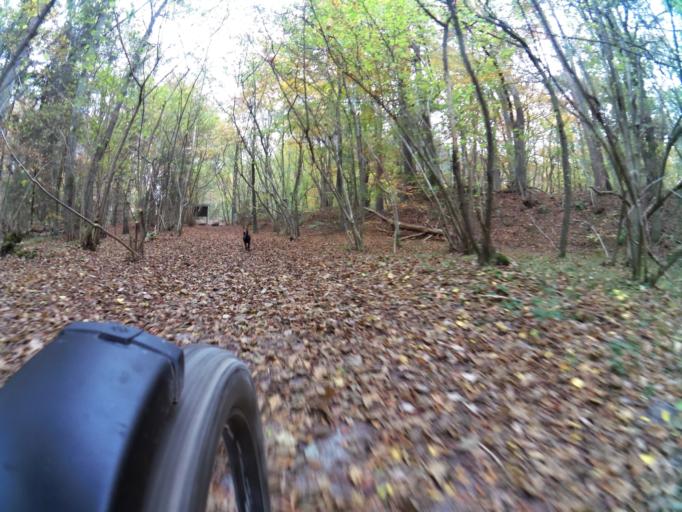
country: PL
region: Pomeranian Voivodeship
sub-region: Powiat pucki
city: Krokowa
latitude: 54.8302
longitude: 18.1436
